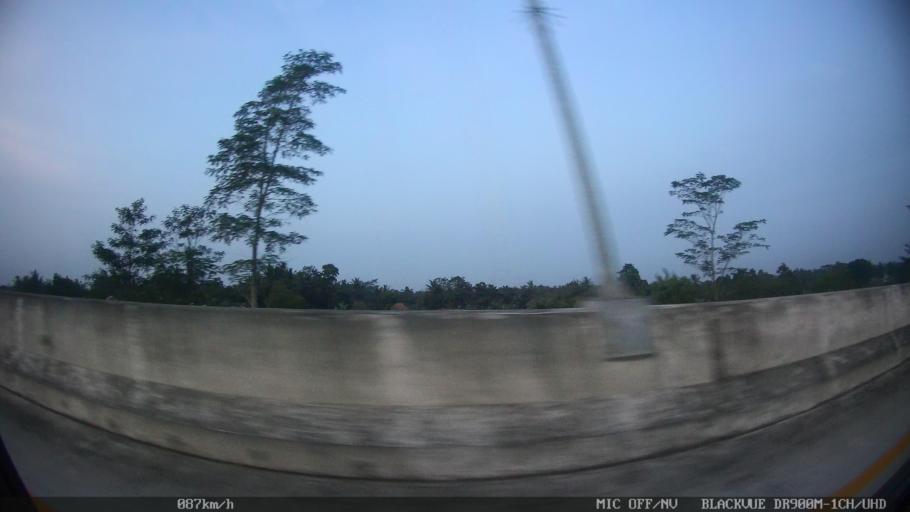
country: ID
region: Lampung
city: Kalianda
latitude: -5.6770
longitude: 105.6064
